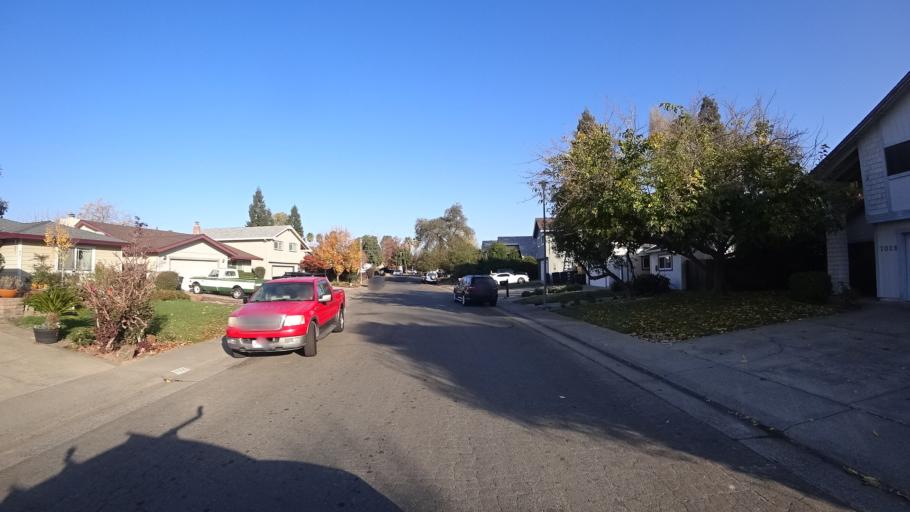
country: US
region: California
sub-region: Sacramento County
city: Citrus Heights
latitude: 38.6947
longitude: -121.2599
